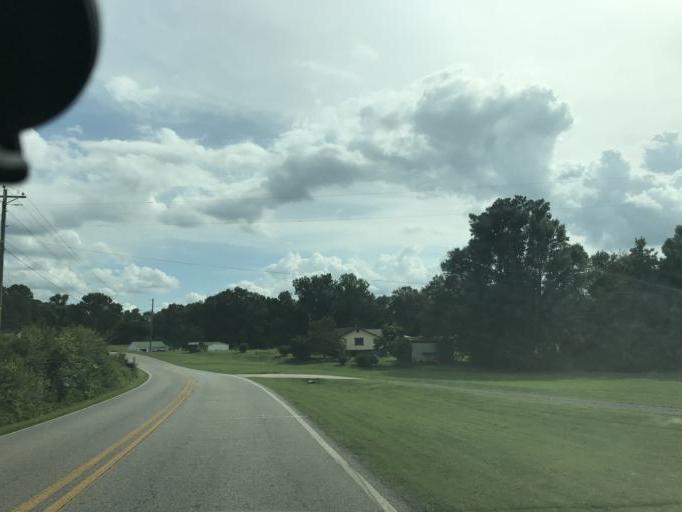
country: US
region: Georgia
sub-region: Forsyth County
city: Cumming
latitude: 34.2654
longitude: -84.1499
